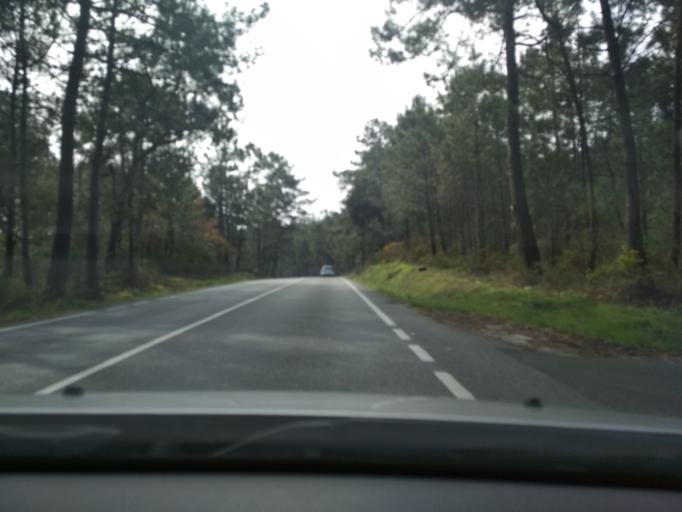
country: ES
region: Galicia
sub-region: Provincia de Pontevedra
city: Catoira
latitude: 42.6743
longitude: -8.7148
